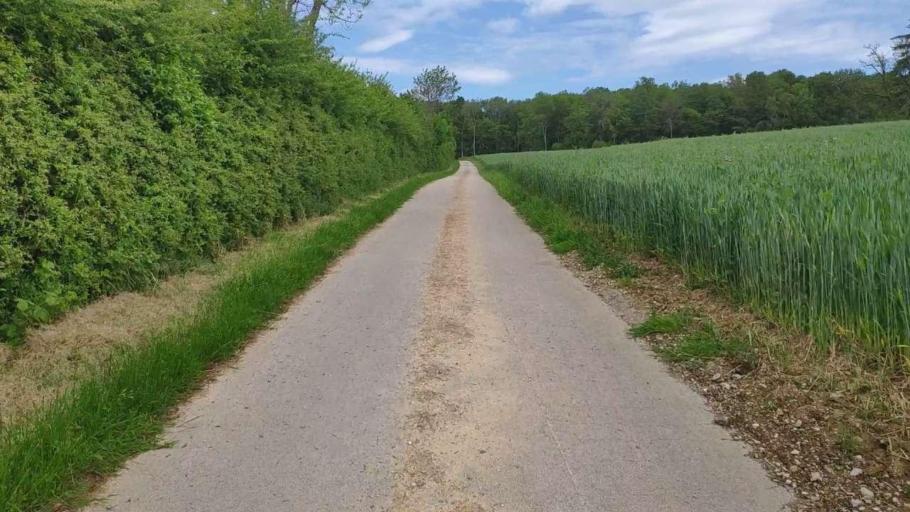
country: FR
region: Franche-Comte
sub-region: Departement du Jura
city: Poligny
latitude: 46.7688
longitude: 5.6563
